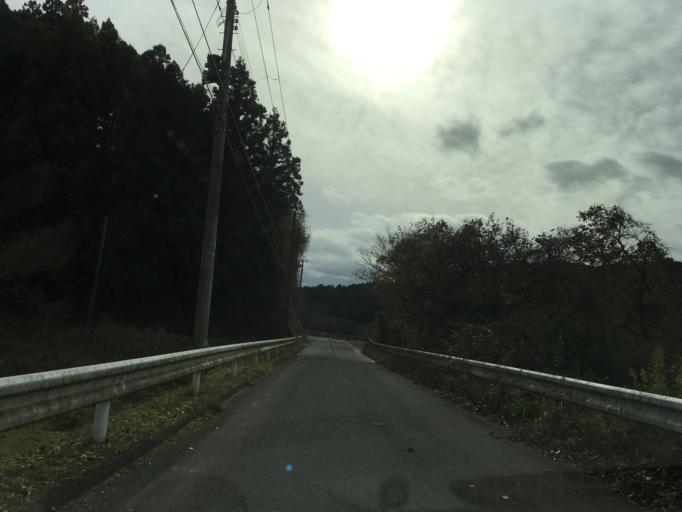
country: JP
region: Iwate
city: Ichinoseki
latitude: 38.7733
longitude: 141.2683
